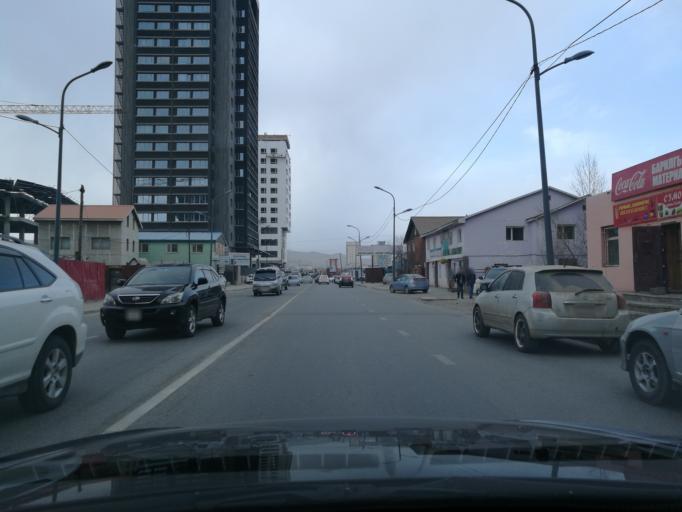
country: MN
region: Ulaanbaatar
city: Ulaanbaatar
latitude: 47.9313
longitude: 106.9139
